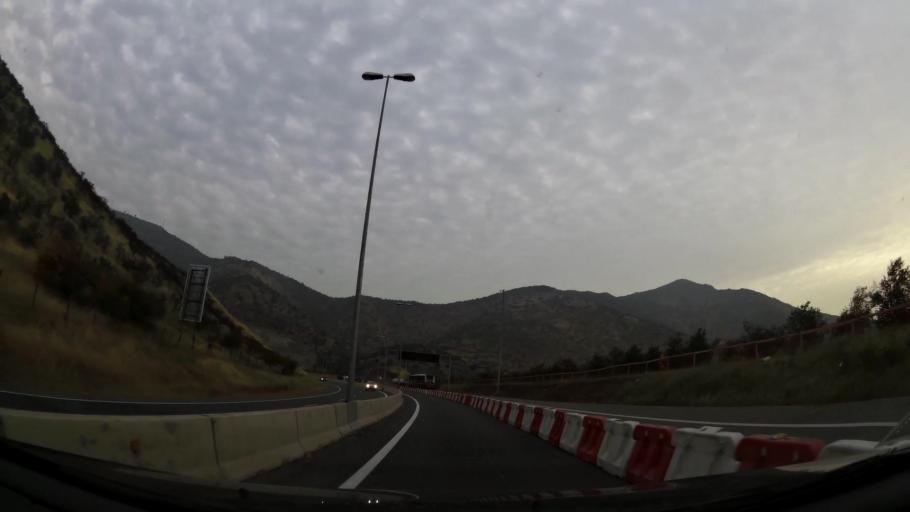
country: CL
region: Santiago Metropolitan
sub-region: Provincia de Chacabuco
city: Chicureo Abajo
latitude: -33.3306
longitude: -70.6280
